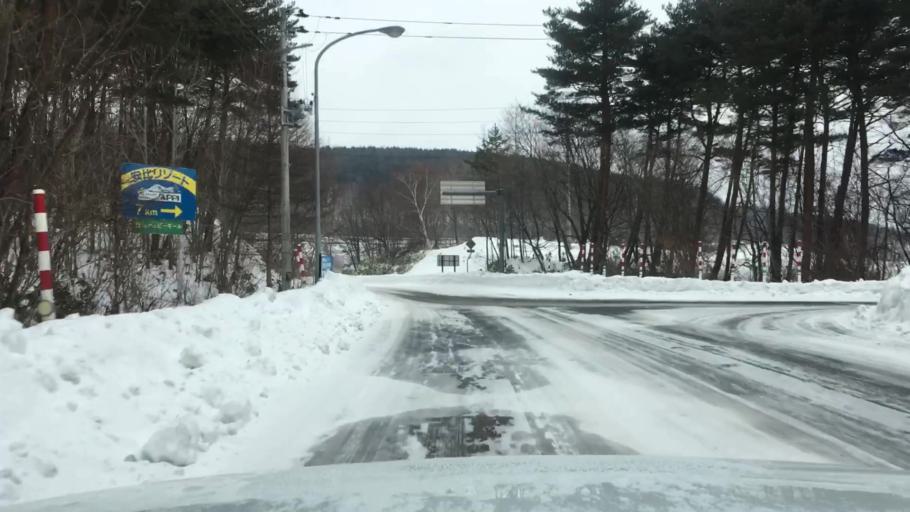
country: JP
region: Iwate
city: Shizukuishi
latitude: 39.9479
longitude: 140.9985
